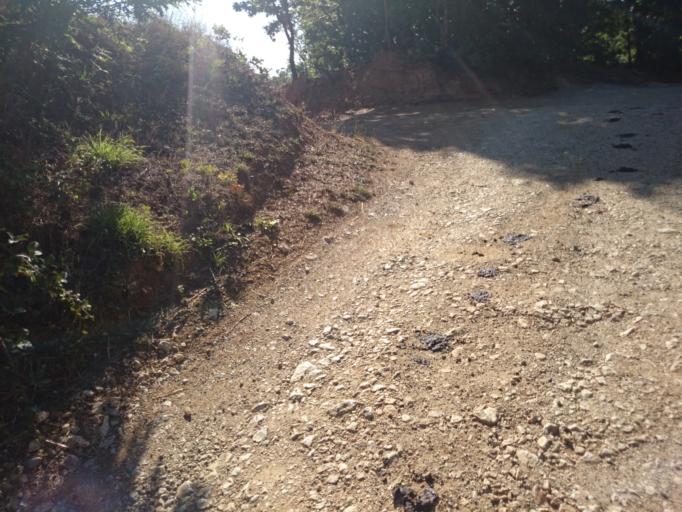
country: AL
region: Diber
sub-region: Rrethi i Bulqizes
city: Zerqan
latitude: 41.5001
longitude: 20.3841
